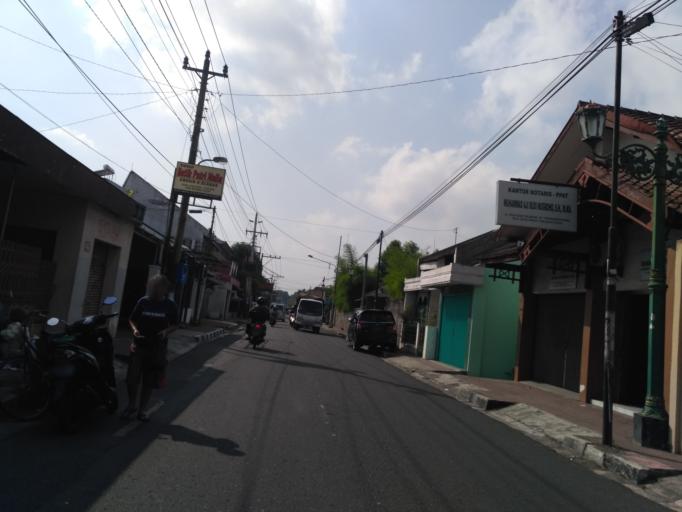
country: ID
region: Daerah Istimewa Yogyakarta
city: Yogyakarta
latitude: -7.8043
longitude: 110.3582
